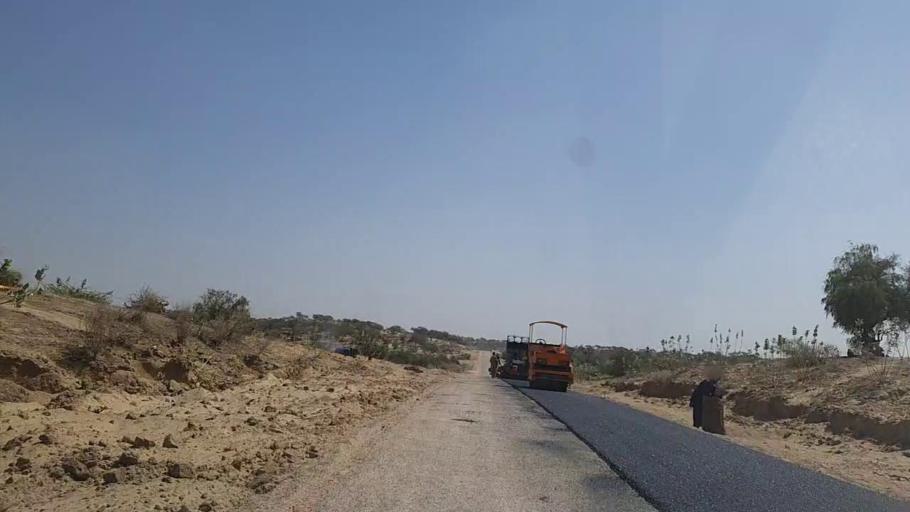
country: PK
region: Sindh
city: Diplo
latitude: 24.4812
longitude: 69.4950
